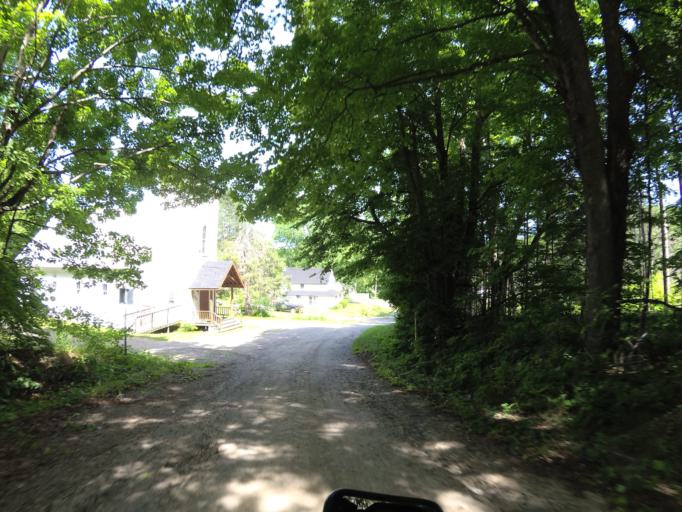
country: CA
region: Ontario
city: Skatepark
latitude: 44.7306
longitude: -76.8429
